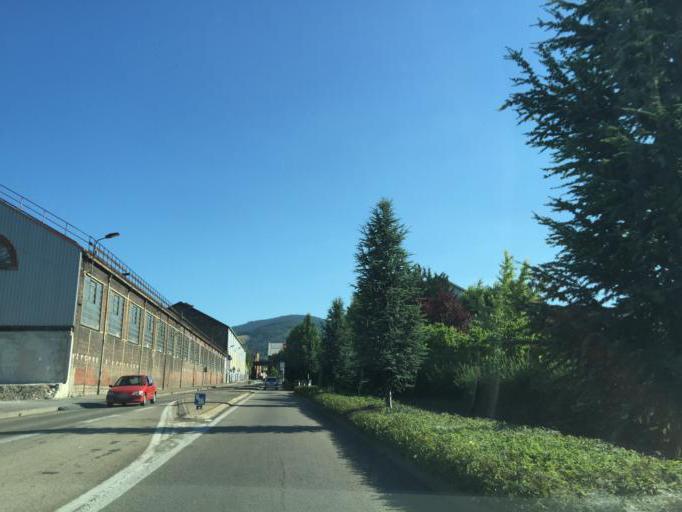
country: FR
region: Rhone-Alpes
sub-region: Departement de la Loire
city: Saint-Chamond
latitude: 45.4689
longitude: 4.5093
